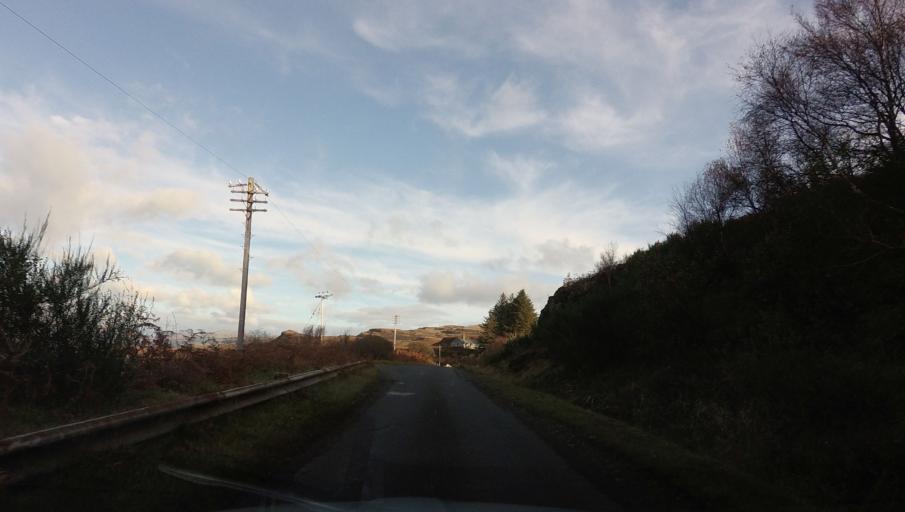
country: GB
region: Scotland
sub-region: Argyll and Bute
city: Isle Of Mull
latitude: 56.3364
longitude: -6.1529
